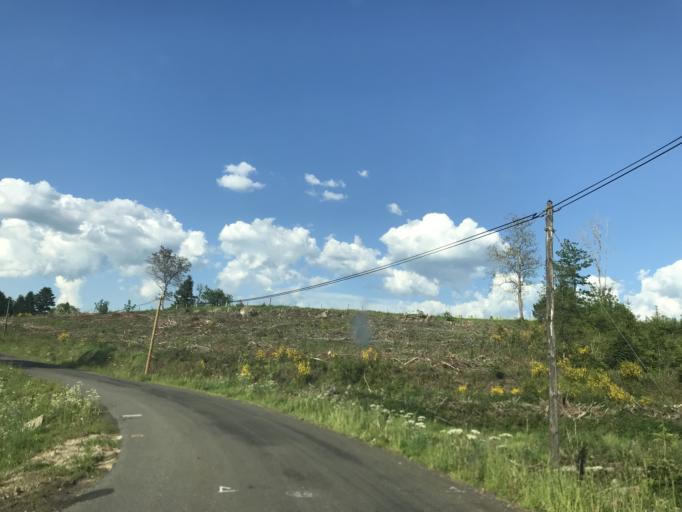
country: FR
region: Auvergne
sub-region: Departement du Puy-de-Dome
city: Job
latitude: 45.6145
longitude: 3.6769
